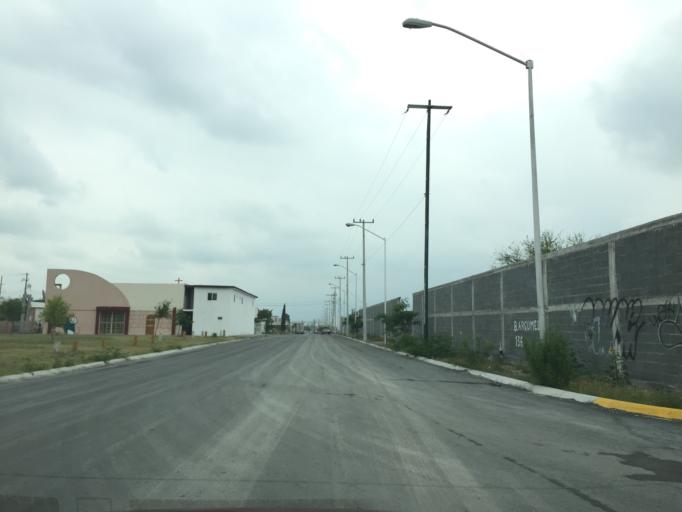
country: MX
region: Nuevo Leon
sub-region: Apodaca
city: Fraccionamiento Cosmopolis Octavo Sector
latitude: 25.8179
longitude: -100.2467
